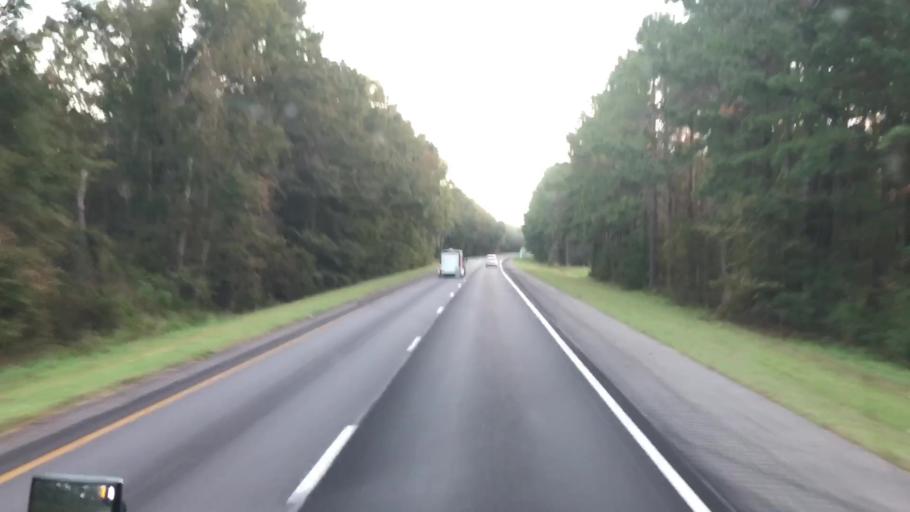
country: US
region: South Carolina
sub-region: Orangeburg County
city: Holly Hill
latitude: 33.5485
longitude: -80.4087
